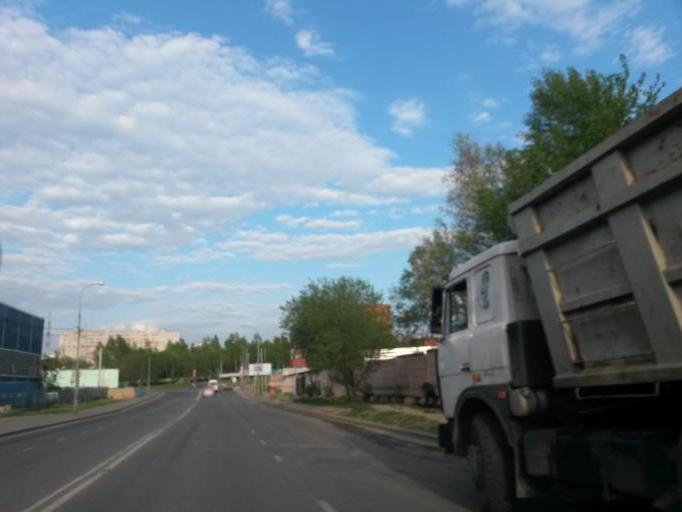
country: RU
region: Moskovskaya
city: Biryulevo Zapadnoye
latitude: 55.5865
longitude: 37.6330
